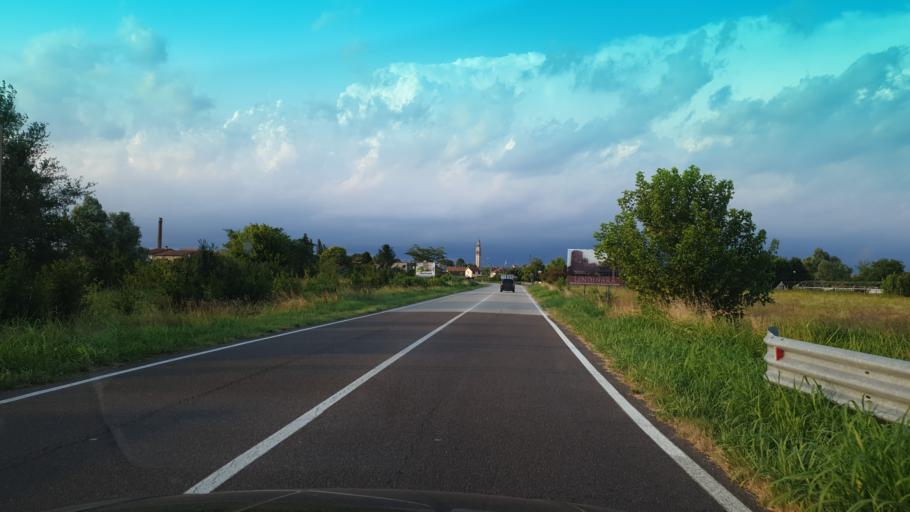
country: IT
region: Veneto
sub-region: Provincia di Rovigo
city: Lendinara
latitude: 45.0723
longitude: 11.5938
